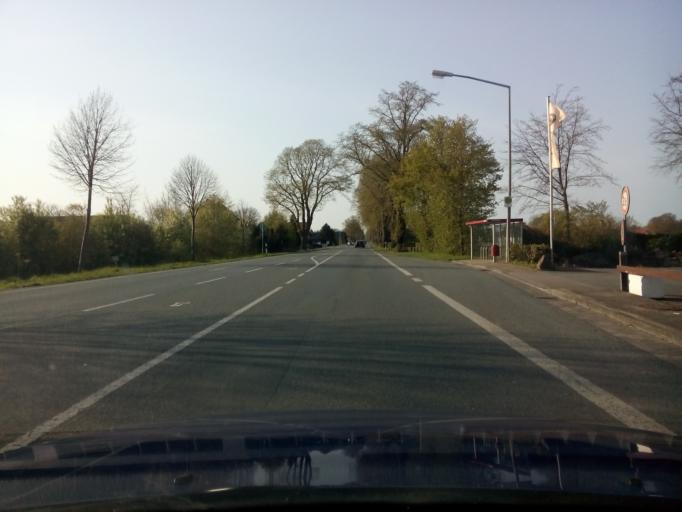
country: DE
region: Lower Saxony
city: Syke
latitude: 52.9632
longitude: 8.7989
